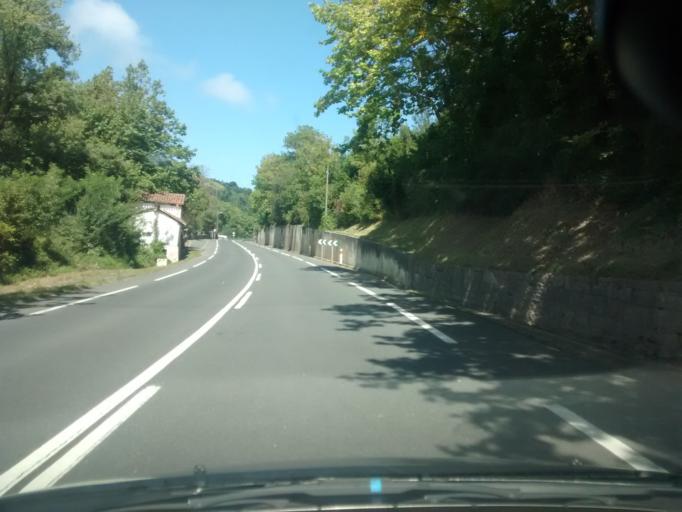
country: ES
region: Basque Country
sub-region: Provincia de Guipuzcoa
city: Zumaia
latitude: 43.2756
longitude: -2.2677
